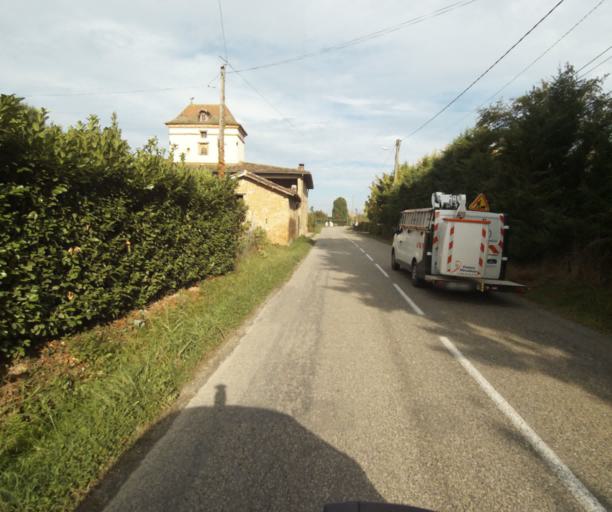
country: FR
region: Midi-Pyrenees
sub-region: Departement du Tarn-et-Garonne
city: Montech
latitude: 43.9678
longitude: 1.2326
